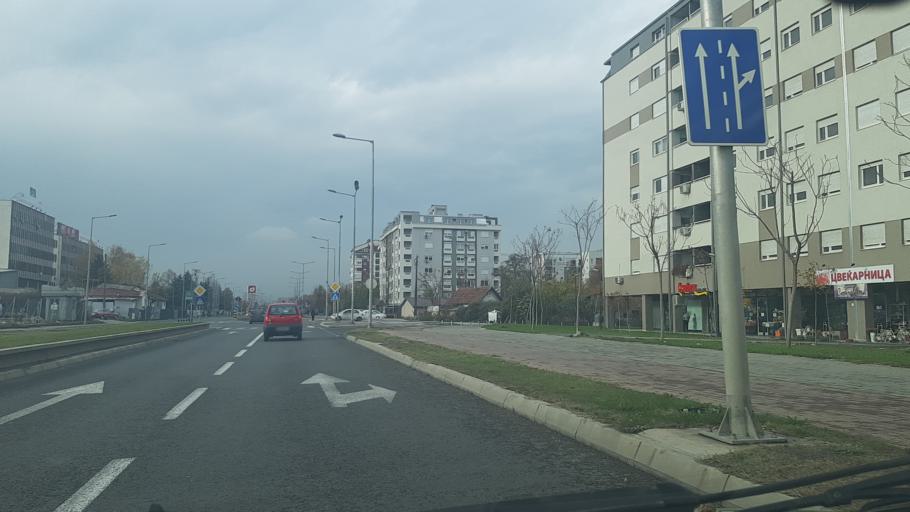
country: MK
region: Kisela Voda
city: Usje
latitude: 41.9807
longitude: 21.4572
